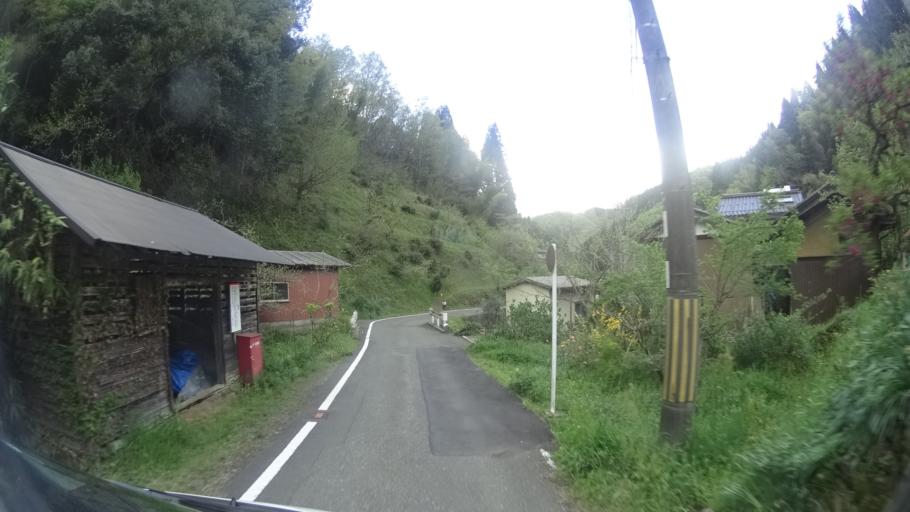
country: JP
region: Kyoto
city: Ayabe
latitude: 35.2566
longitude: 135.3371
